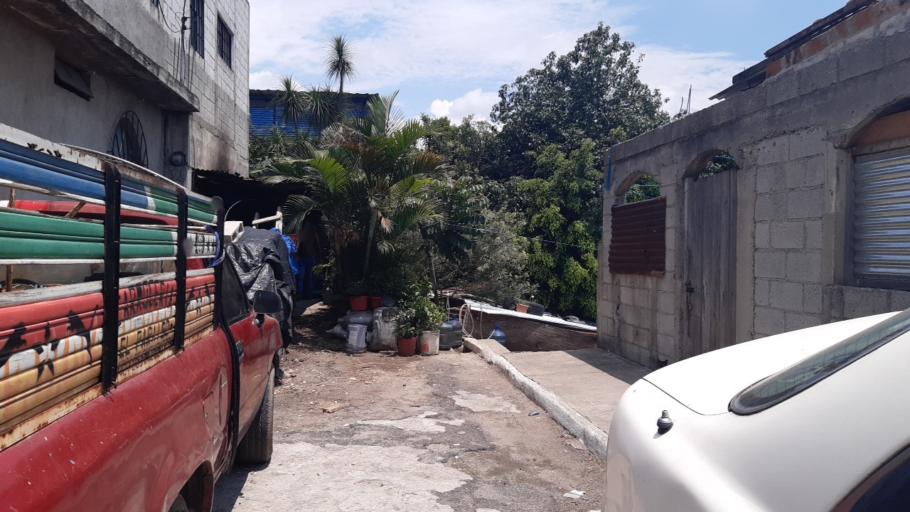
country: GT
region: Guatemala
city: Petapa
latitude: 14.5088
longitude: -90.5599
